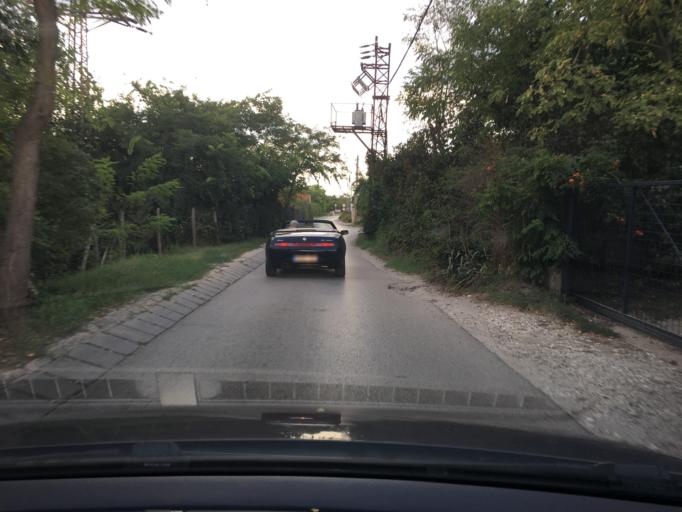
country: HU
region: Pest
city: Szada
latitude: 47.6424
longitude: 19.3081
